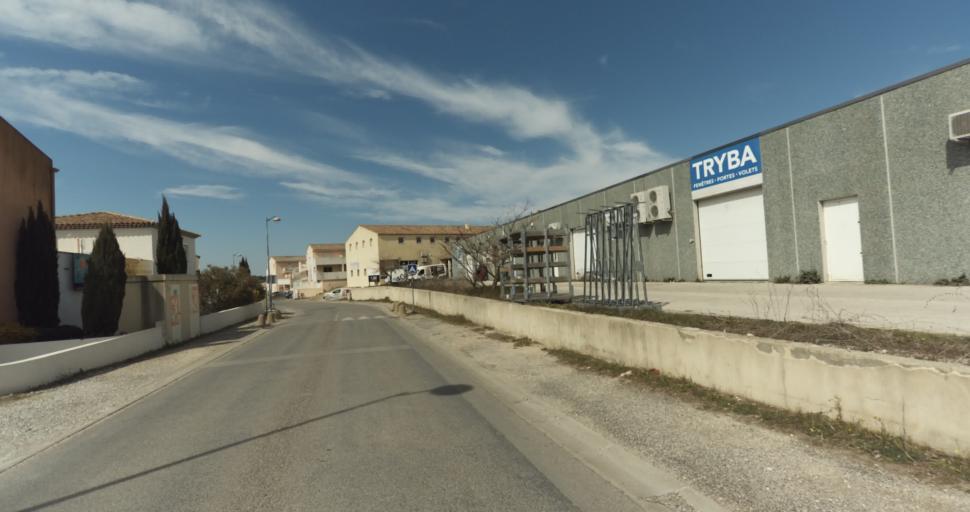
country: FR
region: Provence-Alpes-Cote d'Azur
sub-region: Departement des Bouches-du-Rhone
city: Saint-Cannat
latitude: 43.6147
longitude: 5.3176
